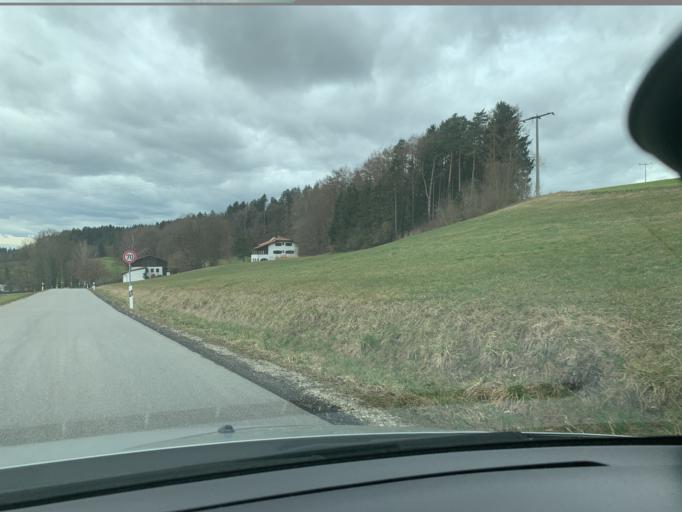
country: DE
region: Bavaria
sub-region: Lower Bavaria
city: Kumhausen
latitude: 48.5179
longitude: 12.1913
